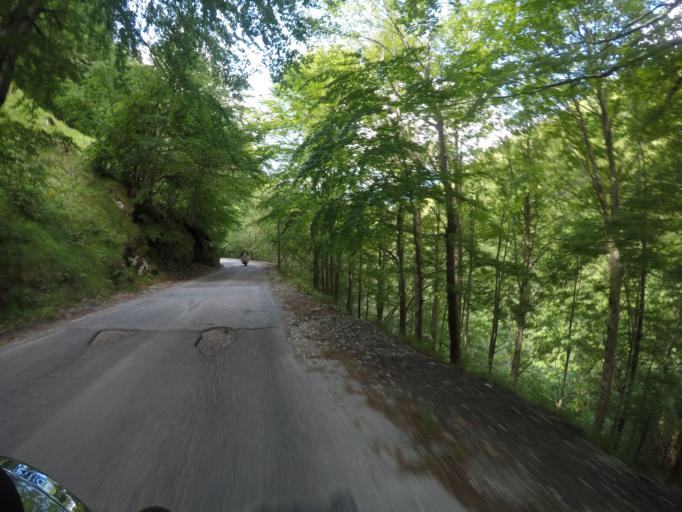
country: IT
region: Tuscany
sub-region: Provincia di Lucca
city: Minucciano
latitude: 44.1421
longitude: 10.1942
